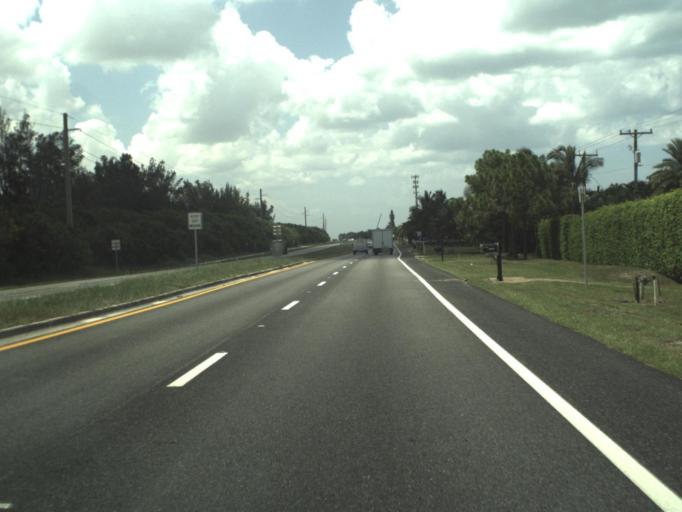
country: US
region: Florida
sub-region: Palm Beach County
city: Tequesta
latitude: 26.9791
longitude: -80.0901
